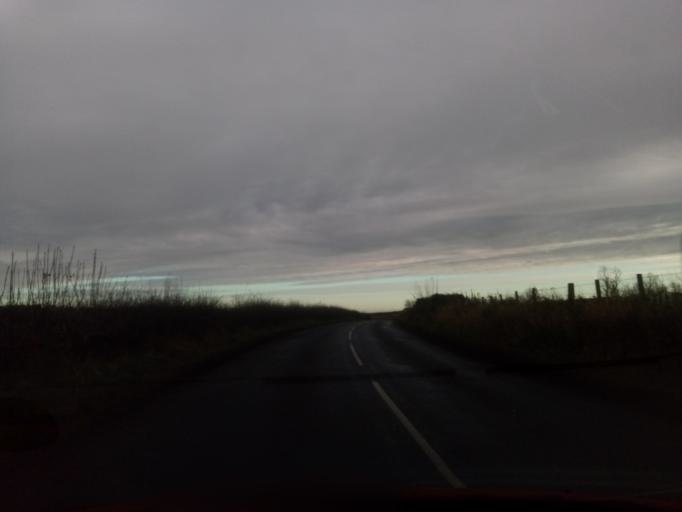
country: GB
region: Scotland
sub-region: The Scottish Borders
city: Saint Boswells
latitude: 55.5652
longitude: -2.6112
